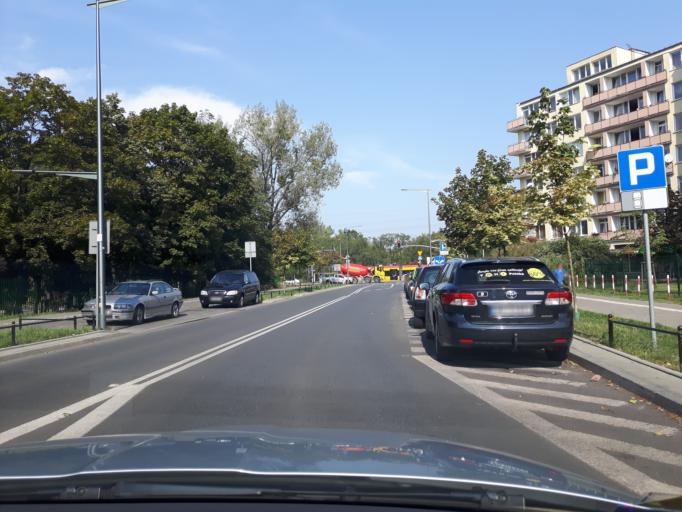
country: PL
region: Masovian Voivodeship
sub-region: Warszawa
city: Praga Polnoc
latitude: 52.2658
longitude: 21.0312
